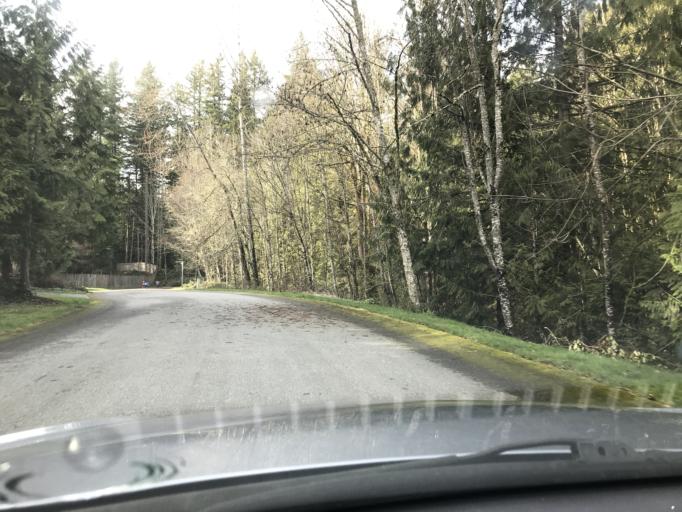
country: US
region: Washington
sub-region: King County
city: Ames Lake
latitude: 47.6363
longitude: -121.9728
